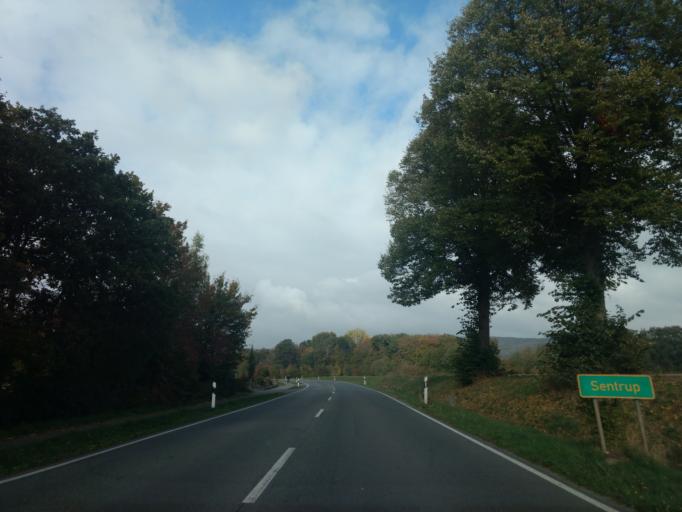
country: DE
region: Lower Saxony
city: Hilter
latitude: 52.1372
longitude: 8.1114
